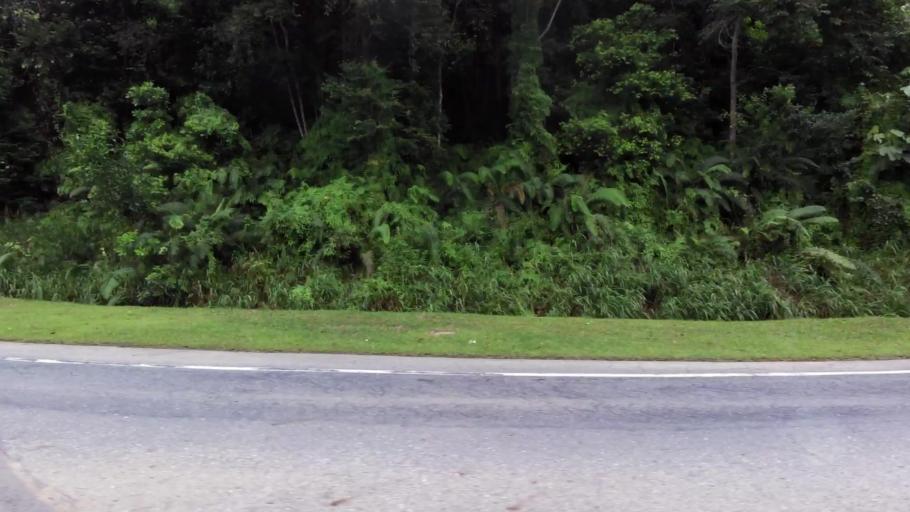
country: BN
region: Brunei and Muara
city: Bandar Seri Begawan
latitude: 4.8815
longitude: 114.9180
